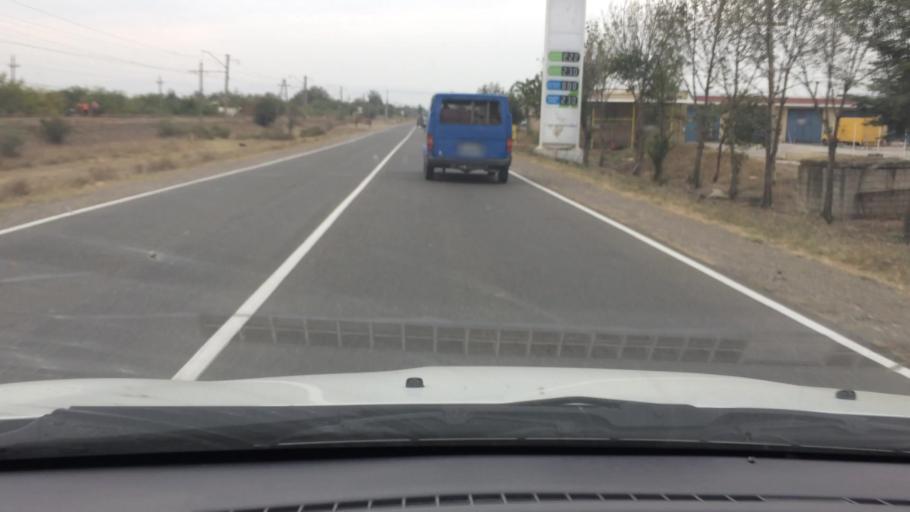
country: GE
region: Kvemo Kartli
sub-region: Marneuli
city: Marneuli
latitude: 41.4383
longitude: 44.8183
